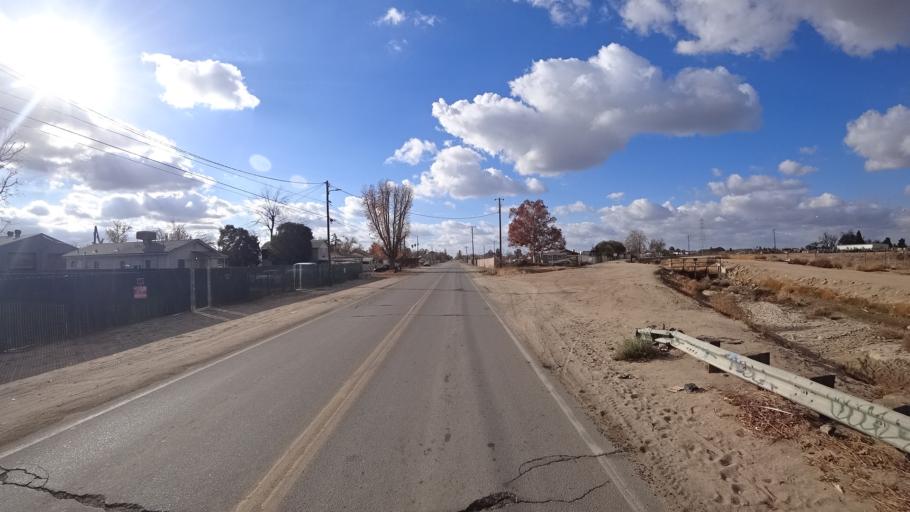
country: US
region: California
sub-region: Kern County
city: Greenfield
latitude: 35.3104
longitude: -118.9920
